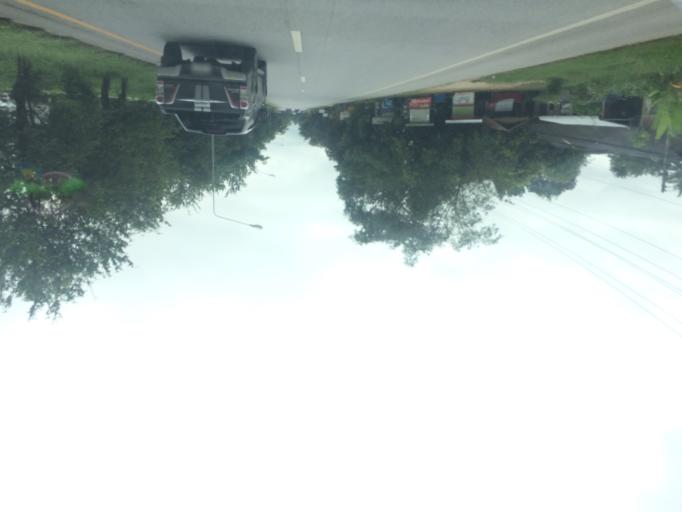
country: TH
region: Chiang Rai
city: Mae Lao
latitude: 19.7665
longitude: 99.7358
